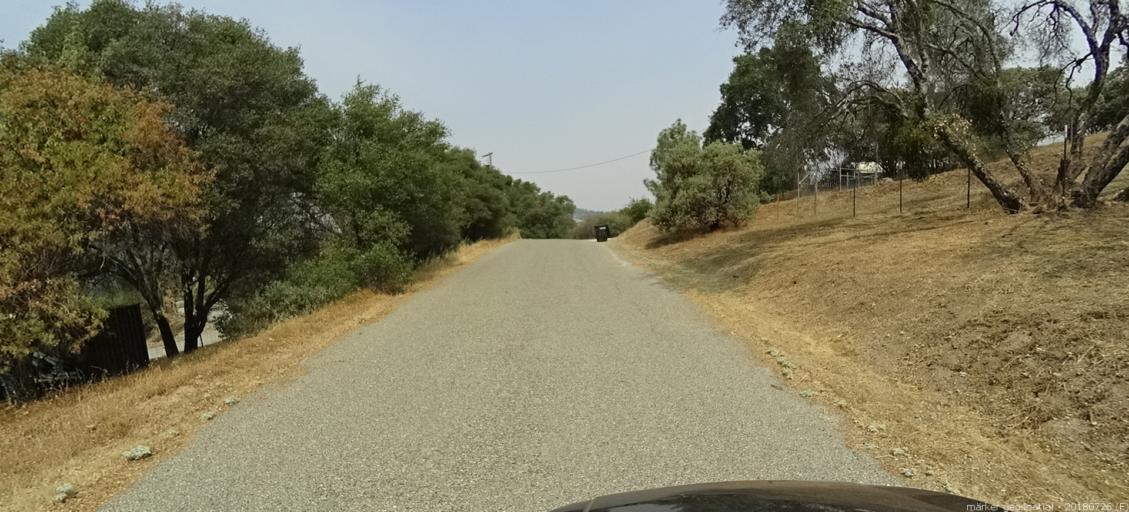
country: US
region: California
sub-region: Madera County
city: Coarsegold
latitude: 37.2447
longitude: -119.7042
